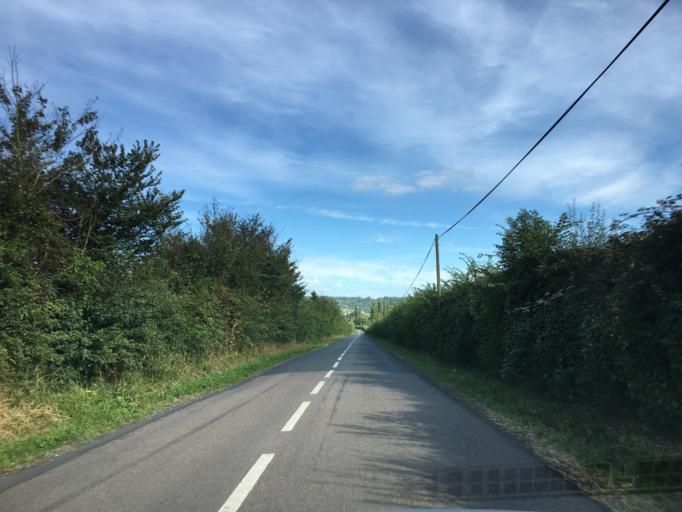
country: FR
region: Lower Normandy
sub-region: Departement du Calvados
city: Dozule
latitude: 49.1693
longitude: -0.0282
